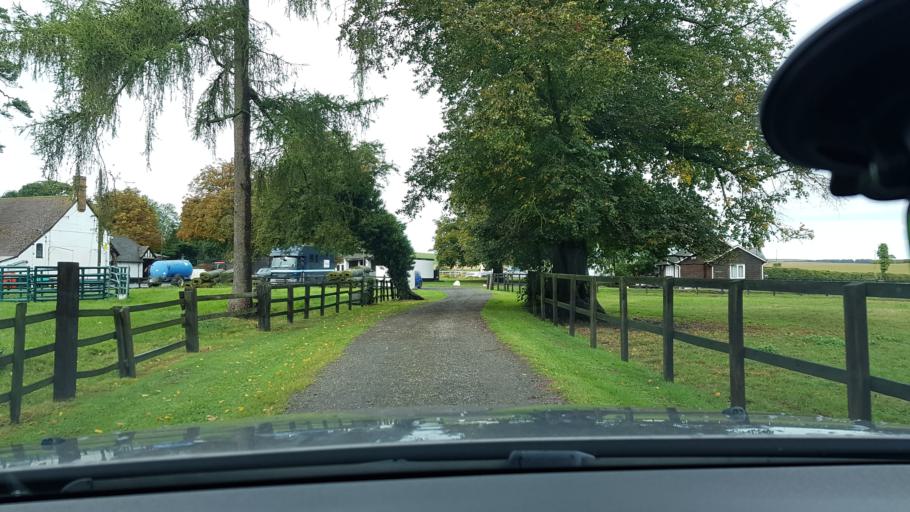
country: GB
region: England
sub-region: West Berkshire
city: Lambourn
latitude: 51.5445
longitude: -1.5327
